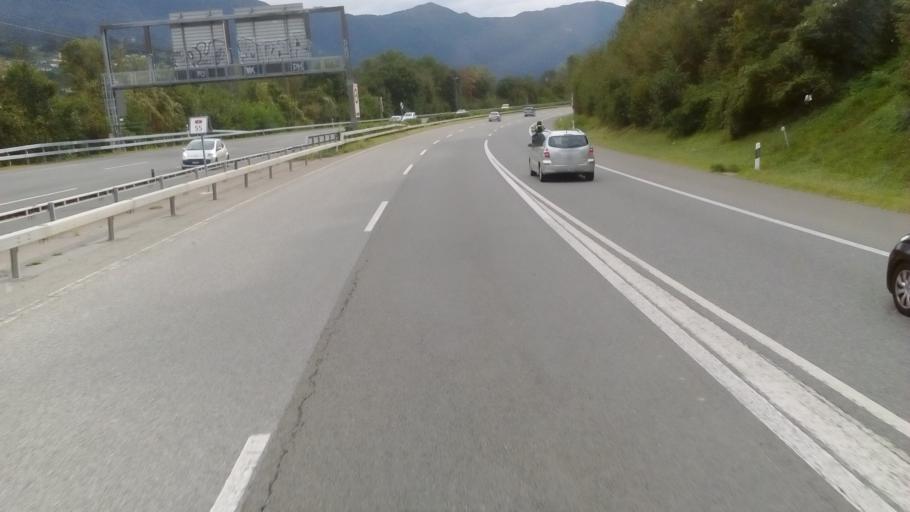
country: CH
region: Ticino
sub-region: Bellinzona District
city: Bellinzona
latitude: 46.2132
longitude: 9.0362
